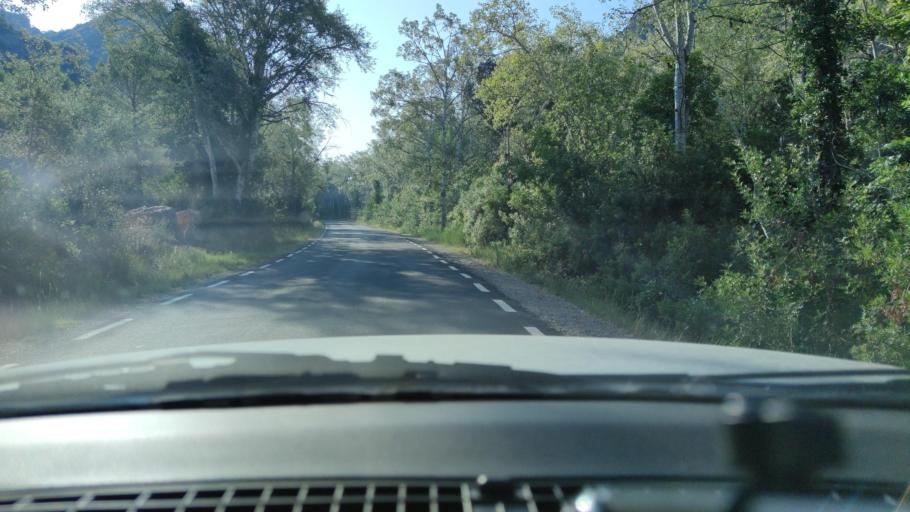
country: ES
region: Catalonia
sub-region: Provincia de Lleida
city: Camarasa
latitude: 41.8728
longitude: 0.8534
